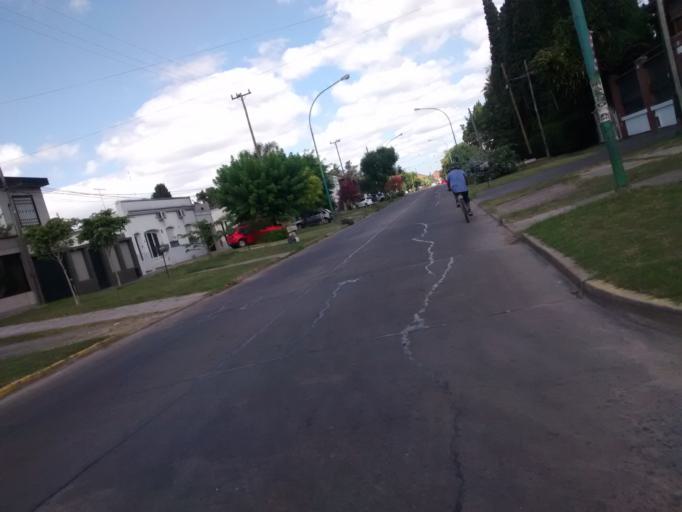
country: AR
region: Buenos Aires
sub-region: Partido de La Plata
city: La Plata
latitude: -34.9401
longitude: -57.9854
